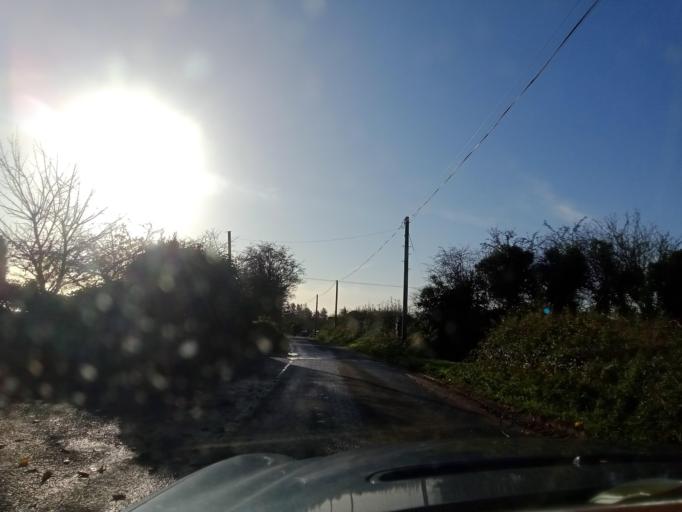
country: IE
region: Leinster
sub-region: Kilkenny
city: Mooncoin
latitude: 52.2807
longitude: -7.2384
